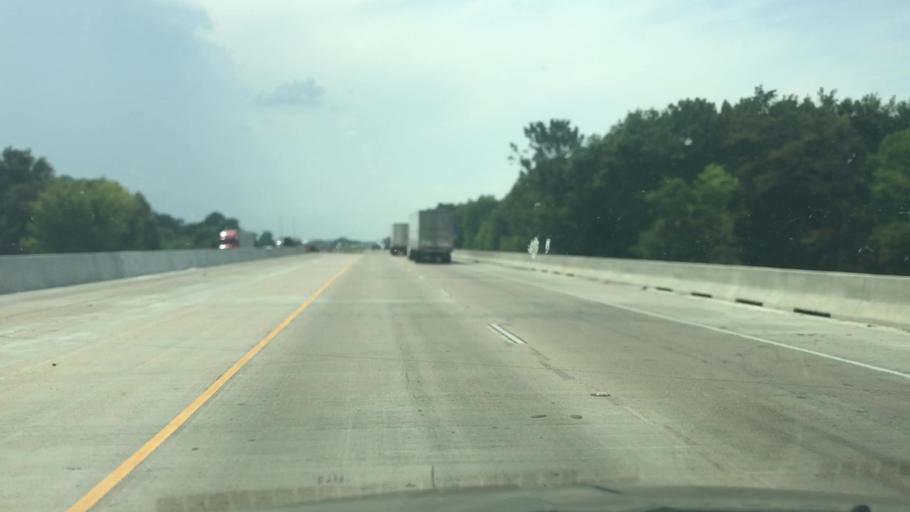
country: US
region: Arkansas
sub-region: Crittenden County
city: Earle
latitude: 35.1339
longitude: -90.4533
